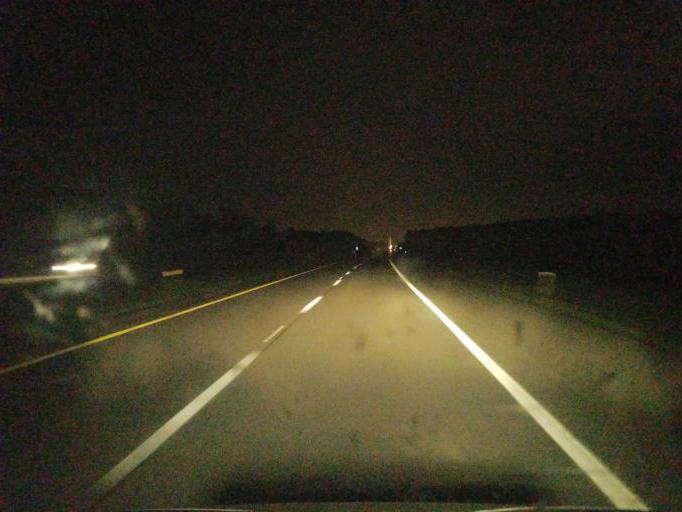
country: US
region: Ohio
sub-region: Geauga County
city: Bainbridge
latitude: 41.3811
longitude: -81.2852
